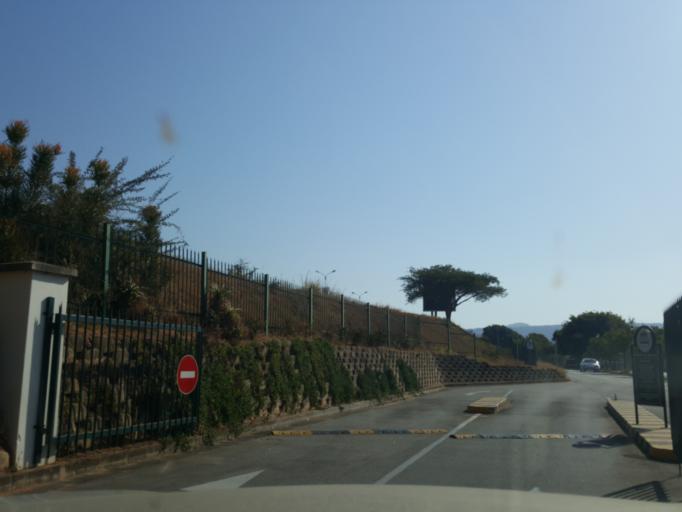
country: ZA
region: Mpumalanga
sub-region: Ehlanzeni District
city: Nelspruit
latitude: -25.4386
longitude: 30.9656
